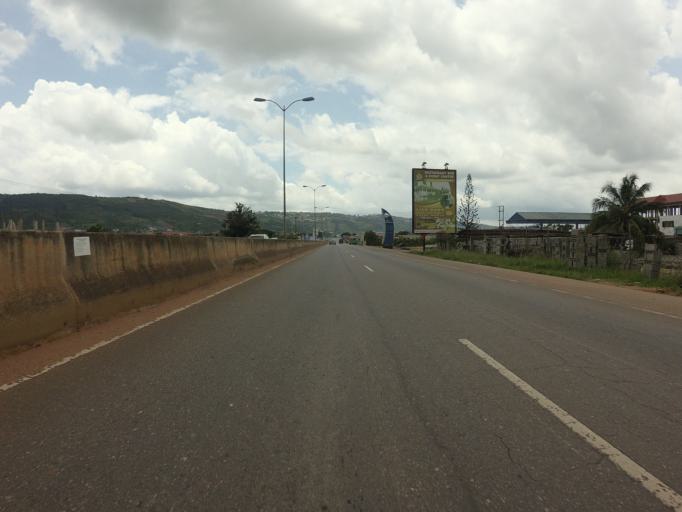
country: GH
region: Eastern
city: Aburi
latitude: 5.7684
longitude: -0.1803
